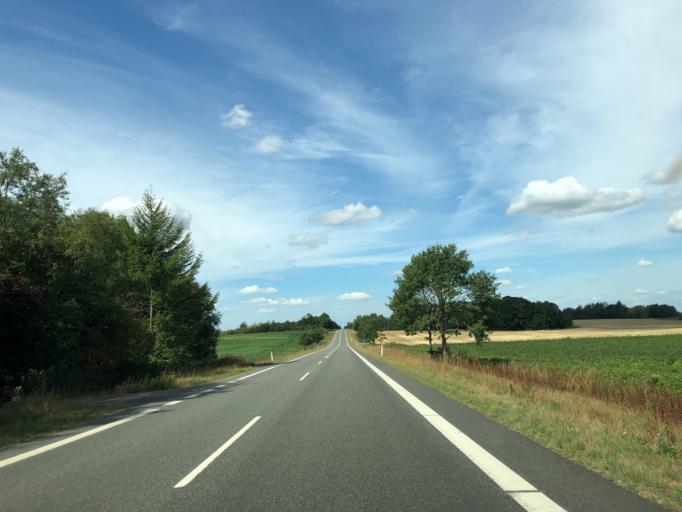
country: DK
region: Central Jutland
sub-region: Ikast-Brande Kommune
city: Bording Kirkeby
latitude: 56.1384
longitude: 9.3135
